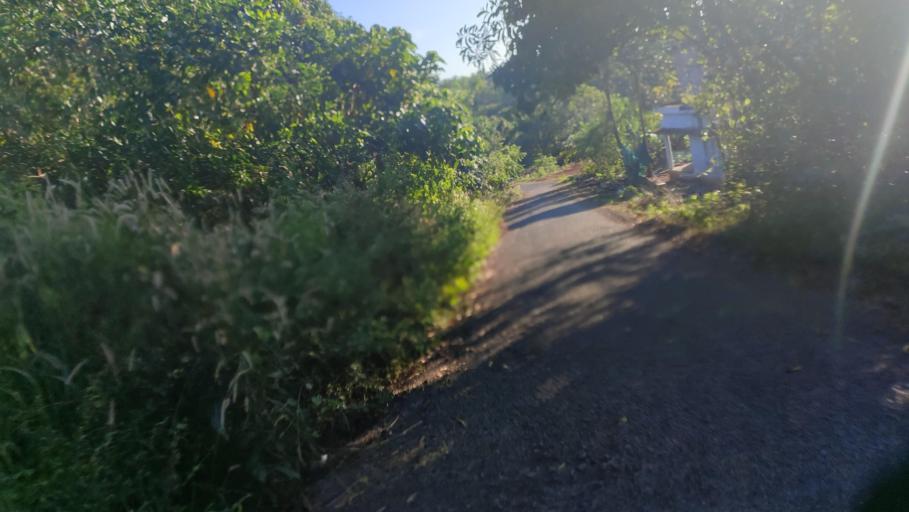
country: IN
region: Kerala
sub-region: Kasaragod District
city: Kasaragod
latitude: 12.5039
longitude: 75.0774
